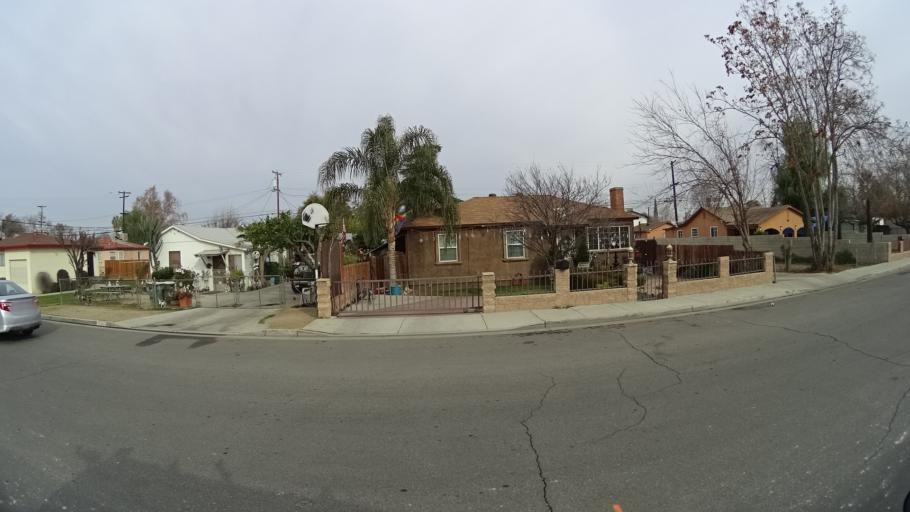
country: US
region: California
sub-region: Kern County
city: Bakersfield
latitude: 35.3589
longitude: -119.0159
